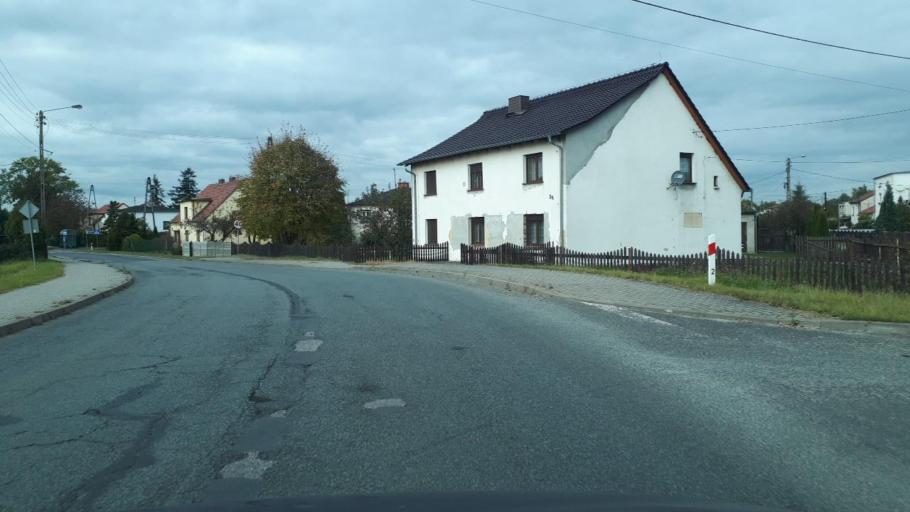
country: PL
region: Opole Voivodeship
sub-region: Powiat strzelecki
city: Zawadzkie
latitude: 50.5817
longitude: 18.5156
